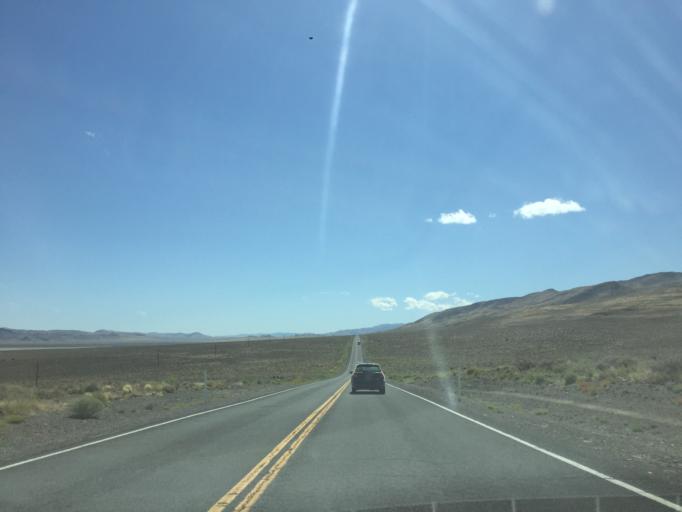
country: US
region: Nevada
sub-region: Lyon County
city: Fernley
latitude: 40.0392
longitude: -119.3853
